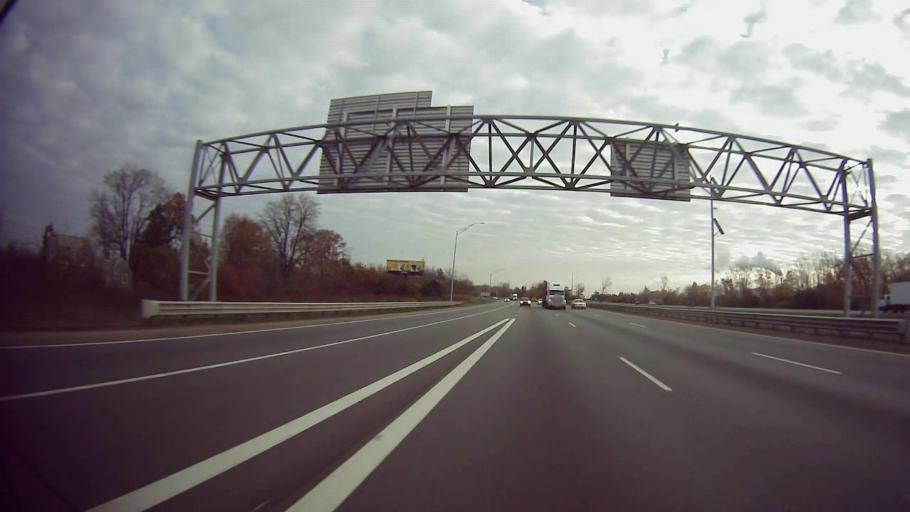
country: US
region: Michigan
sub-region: Wayne County
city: Taylor
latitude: 42.2453
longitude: -83.3176
